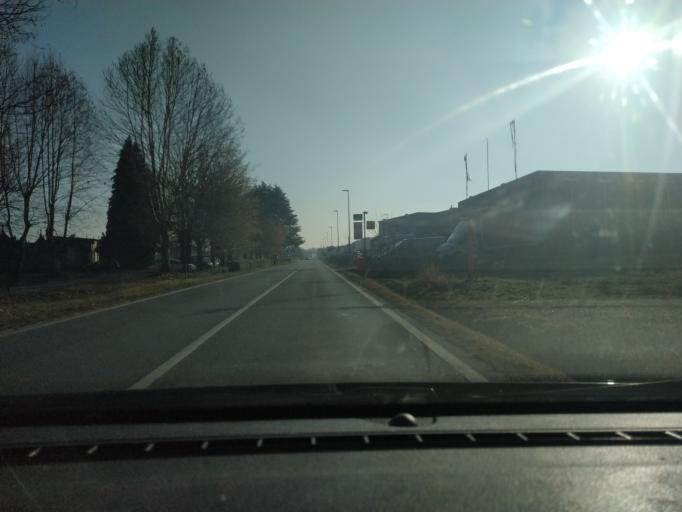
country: IT
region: Piedmont
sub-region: Provincia di Torino
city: Strambino
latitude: 45.3906
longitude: 7.8845
